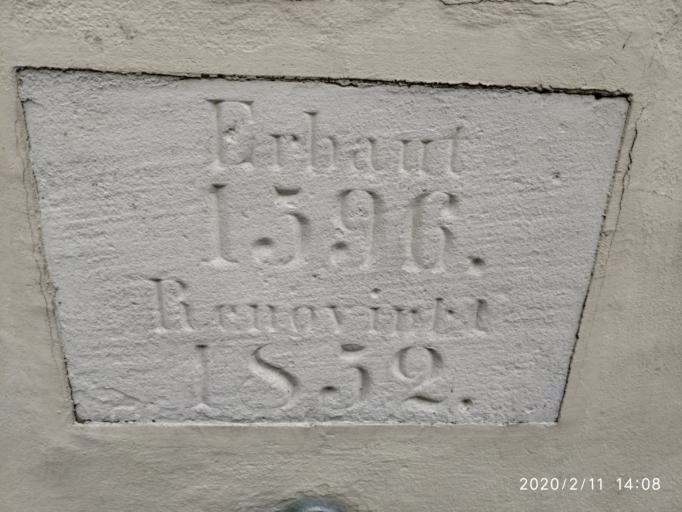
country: PL
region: Lubusz
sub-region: Powiat nowosolski
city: Nowa Sol
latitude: 51.8037
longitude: 15.7199
